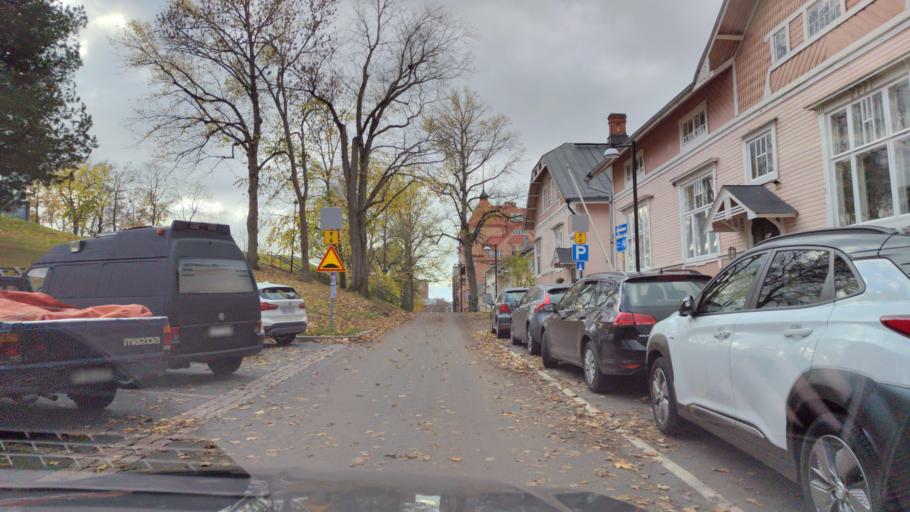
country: FI
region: Varsinais-Suomi
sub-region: Turku
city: Turku
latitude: 60.4547
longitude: 22.2619
